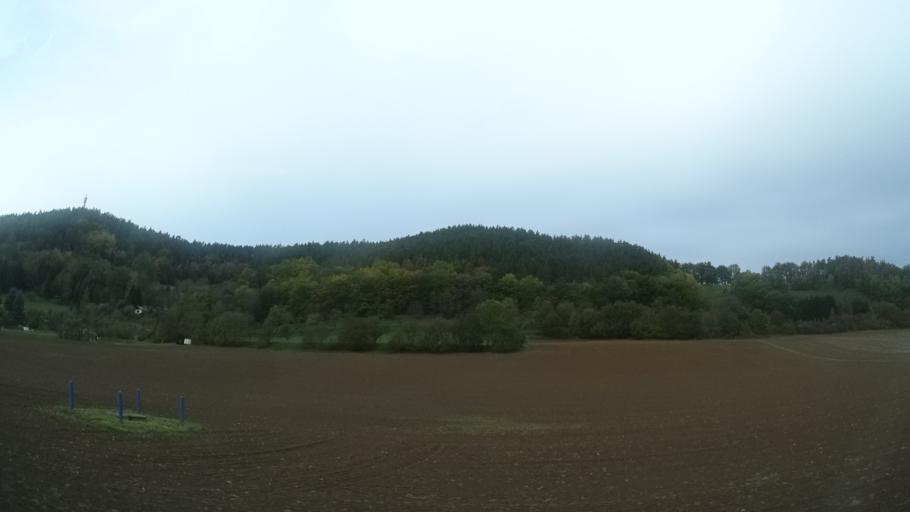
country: DE
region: Thuringia
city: Orlamunde
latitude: 50.7465
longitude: 11.4779
